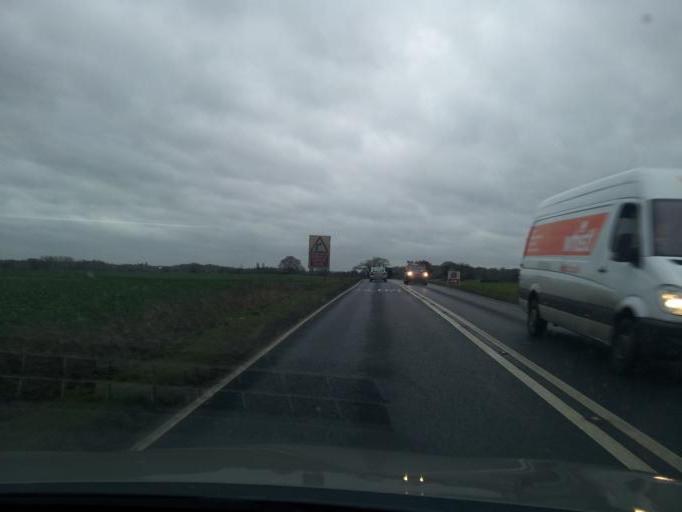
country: GB
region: England
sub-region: Suffolk
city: Thurston
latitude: 52.2772
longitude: 0.7989
